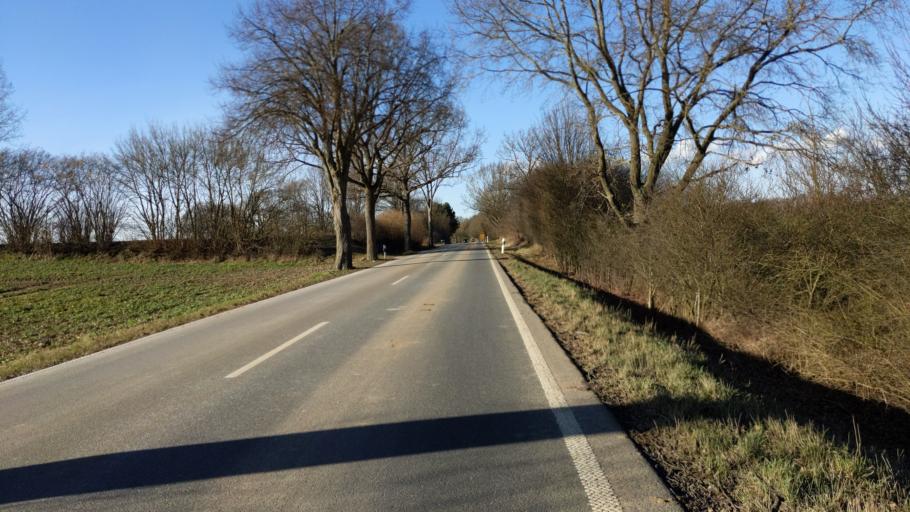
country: DE
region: Schleswig-Holstein
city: Susel
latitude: 54.0601
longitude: 10.6491
